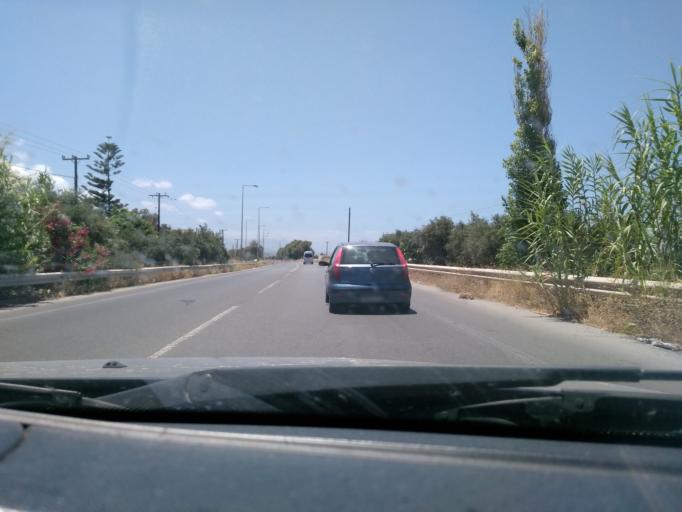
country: GR
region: Crete
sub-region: Nomos Rethymnis
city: Rethymno
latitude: 35.3780
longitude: 24.5722
